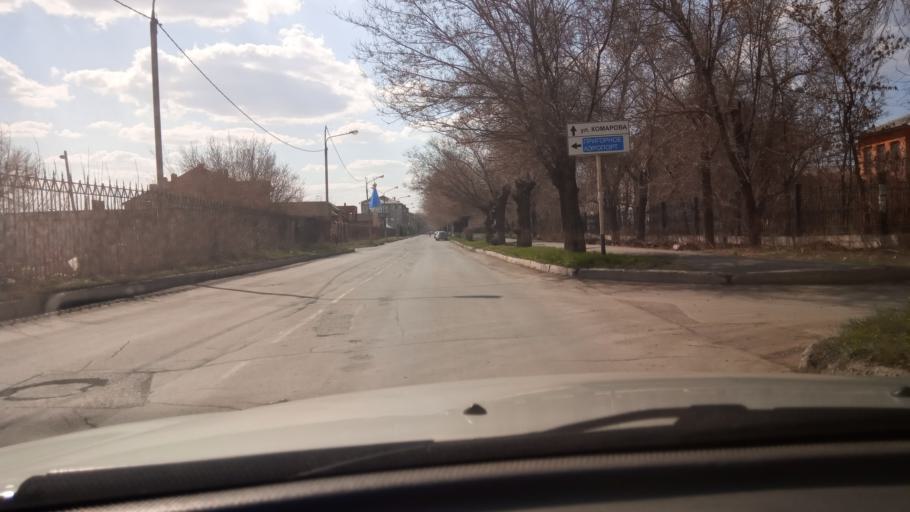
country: RU
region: Orenburg
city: Novotroitsk
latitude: 51.1939
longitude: 58.3125
